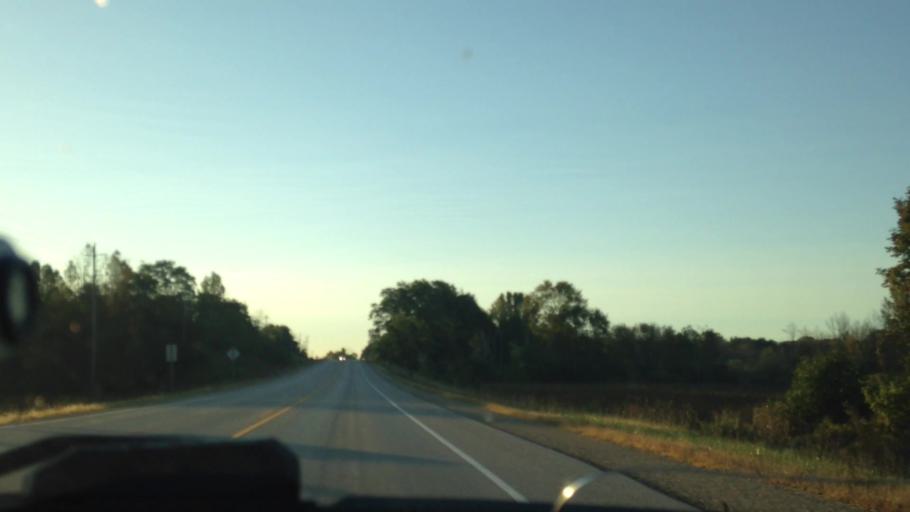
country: US
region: Wisconsin
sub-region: Ozaukee County
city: Saukville
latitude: 43.3953
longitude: -87.9782
